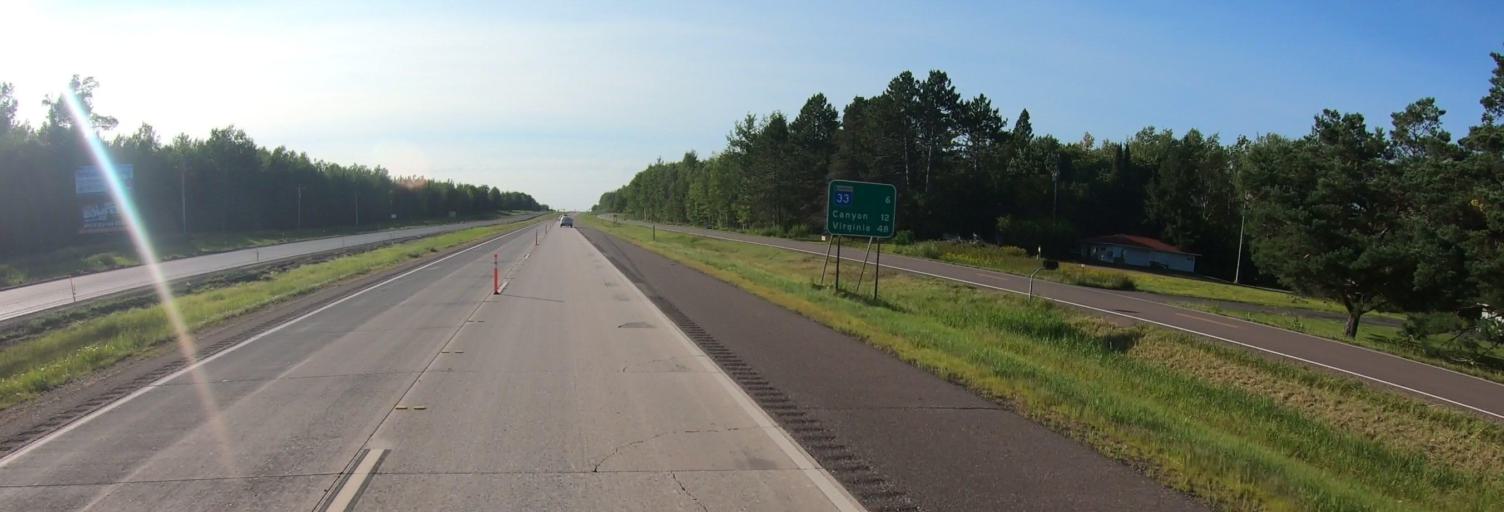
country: US
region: Minnesota
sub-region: Saint Louis County
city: Hermantown
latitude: 46.8971
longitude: -92.3686
